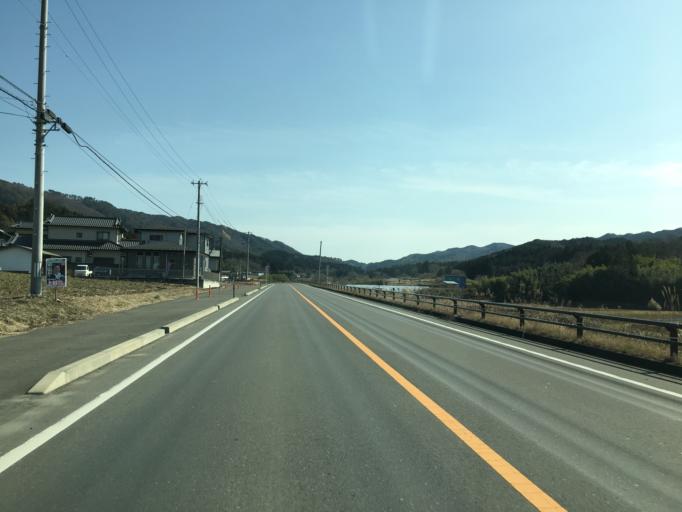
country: JP
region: Ibaraki
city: Daigo
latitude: 36.8356
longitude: 140.4501
